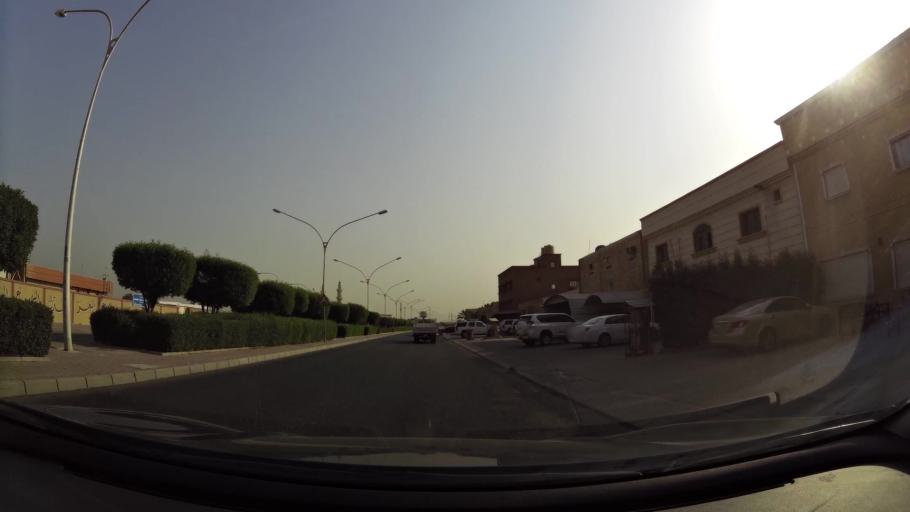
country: KW
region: Al Ahmadi
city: Al Manqaf
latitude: 29.1112
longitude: 48.1056
